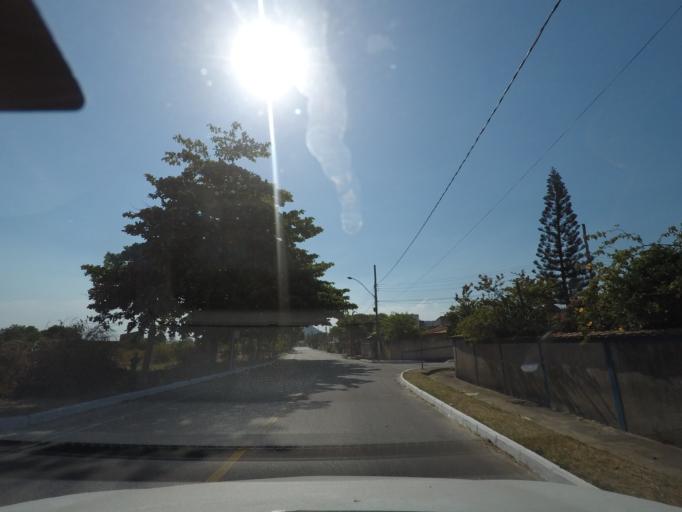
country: BR
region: Rio de Janeiro
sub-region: Niteroi
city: Niteroi
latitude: -22.9672
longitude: -42.9744
